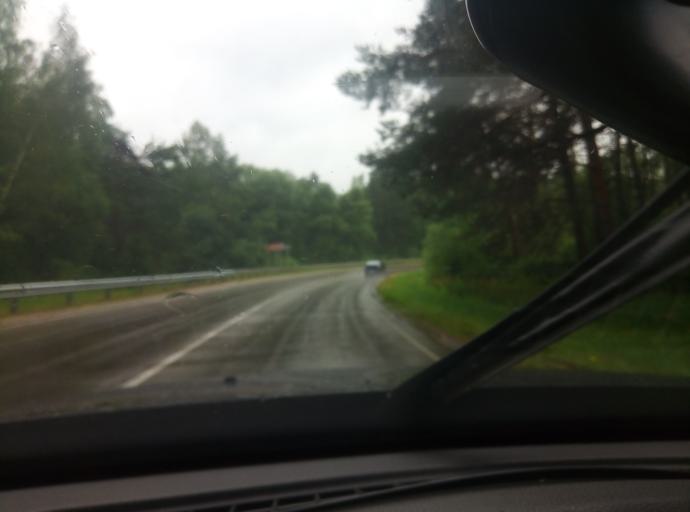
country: RU
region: Kaluga
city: Zhukovo
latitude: 54.9475
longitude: 36.8133
